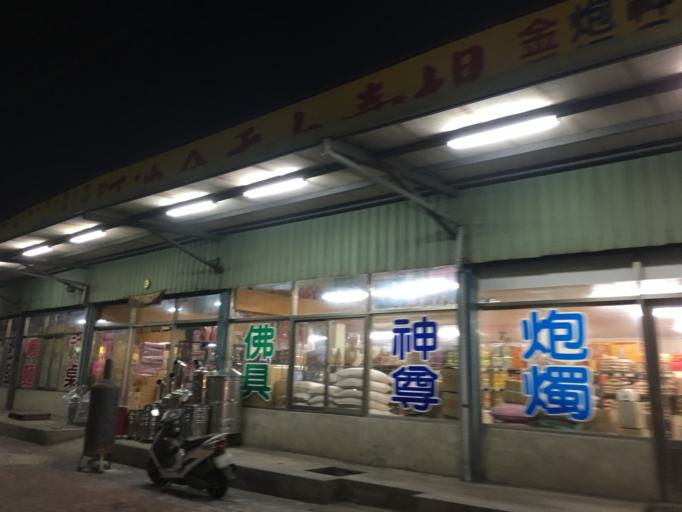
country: TW
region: Taiwan
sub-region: Hsinchu
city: Hsinchu
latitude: 24.7835
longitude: 120.9198
